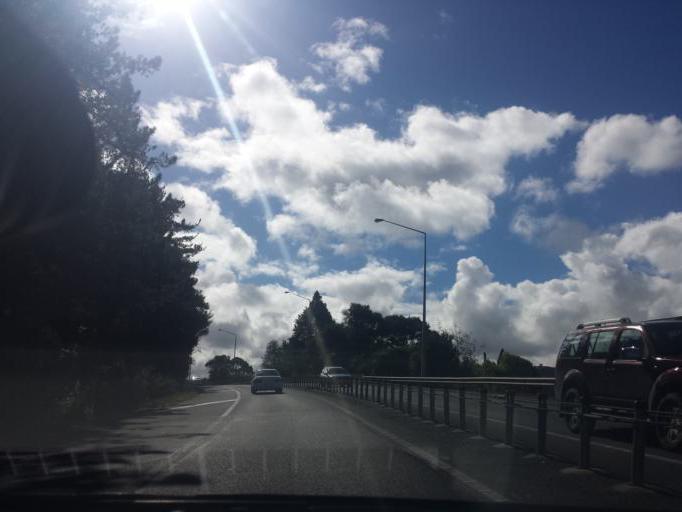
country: NZ
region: Auckland
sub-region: Auckland
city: Warkworth
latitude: -36.5257
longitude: 174.6776
